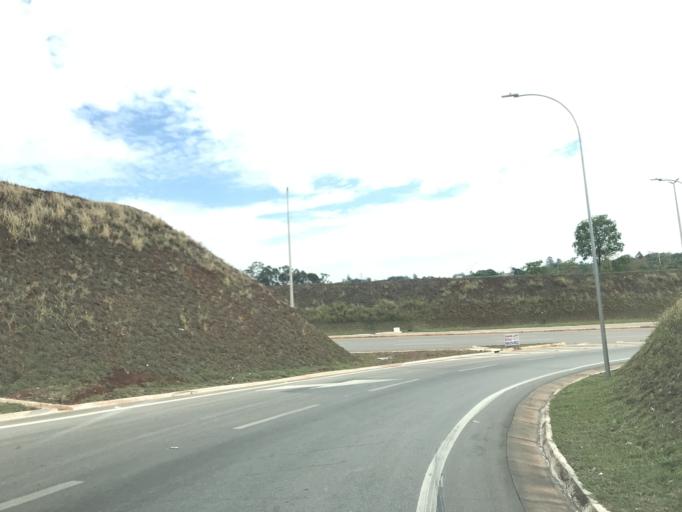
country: BR
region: Federal District
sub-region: Brasilia
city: Brasilia
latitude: -15.7342
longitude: -47.8948
